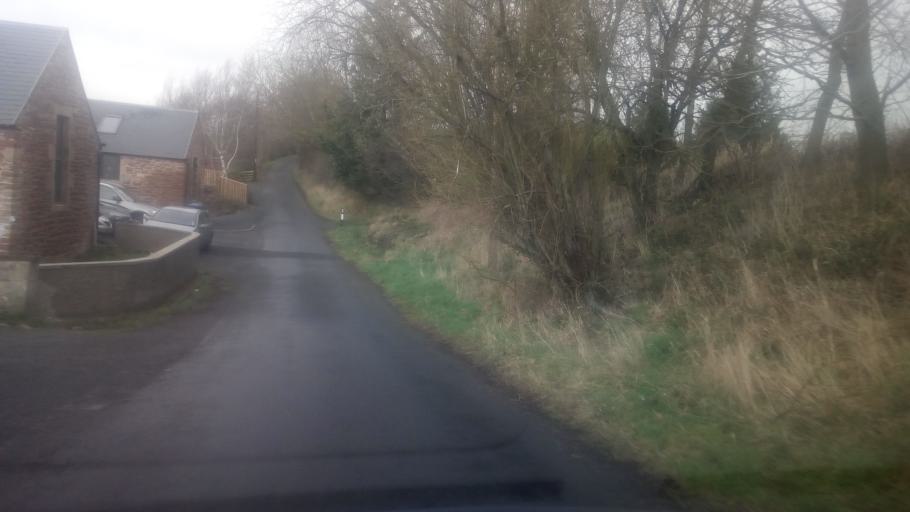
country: GB
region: Scotland
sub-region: The Scottish Borders
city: Jedburgh
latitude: 55.4895
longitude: -2.5412
